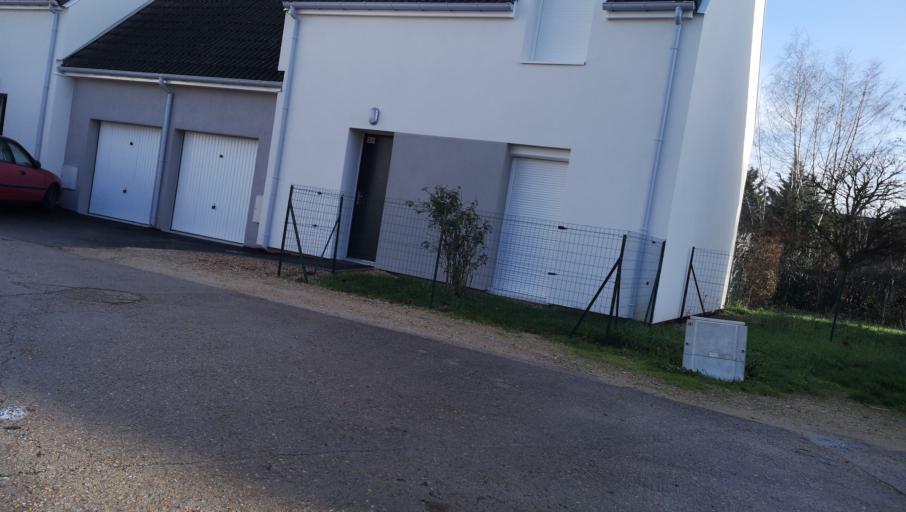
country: FR
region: Centre
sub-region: Departement du Loiret
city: Saint-Pryve-Saint-Mesmin
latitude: 47.8754
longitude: 1.8688
